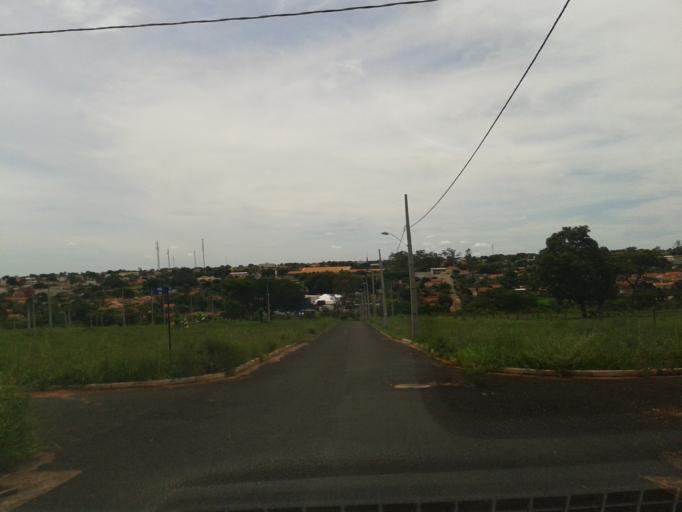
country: BR
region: Minas Gerais
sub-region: Santa Vitoria
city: Santa Vitoria
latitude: -18.8410
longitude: -50.1360
